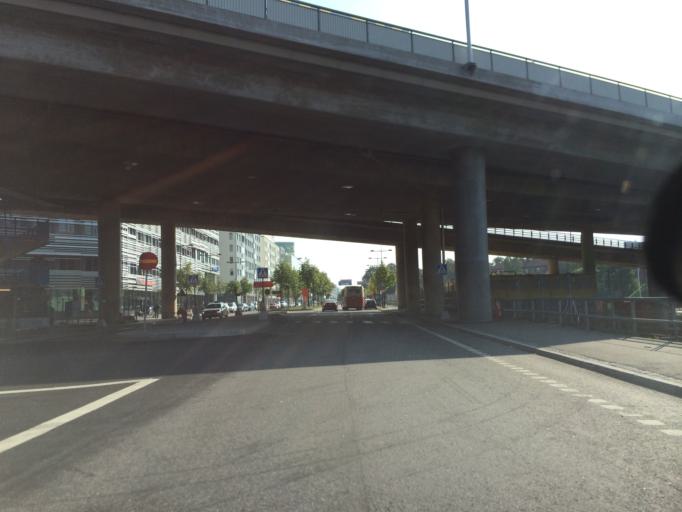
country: SE
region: Stockholm
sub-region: Solna Kommun
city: Solna
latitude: 59.3367
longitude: 18.0099
